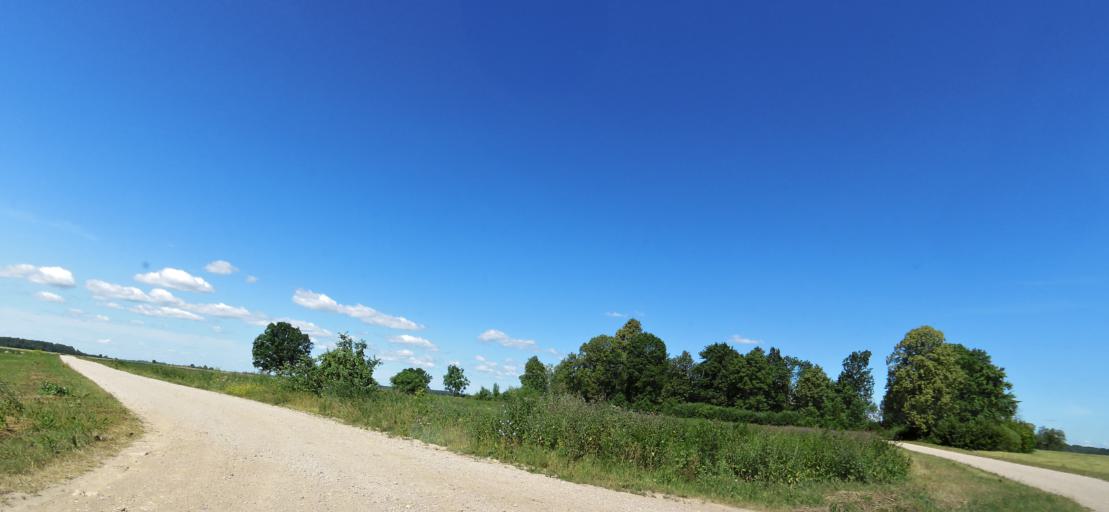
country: LT
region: Panevezys
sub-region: Birzai
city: Birzai
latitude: 56.2596
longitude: 24.5376
